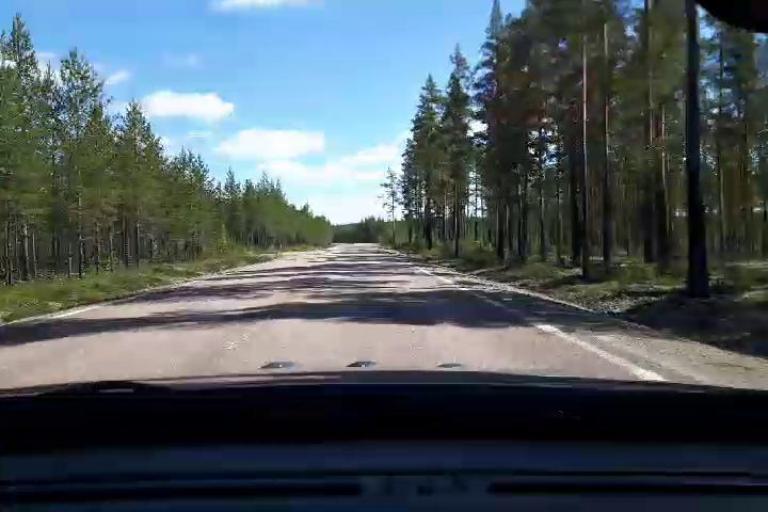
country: SE
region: Gaevleborg
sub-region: Ljusdals Kommun
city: Farila
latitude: 61.9398
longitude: 15.4838
